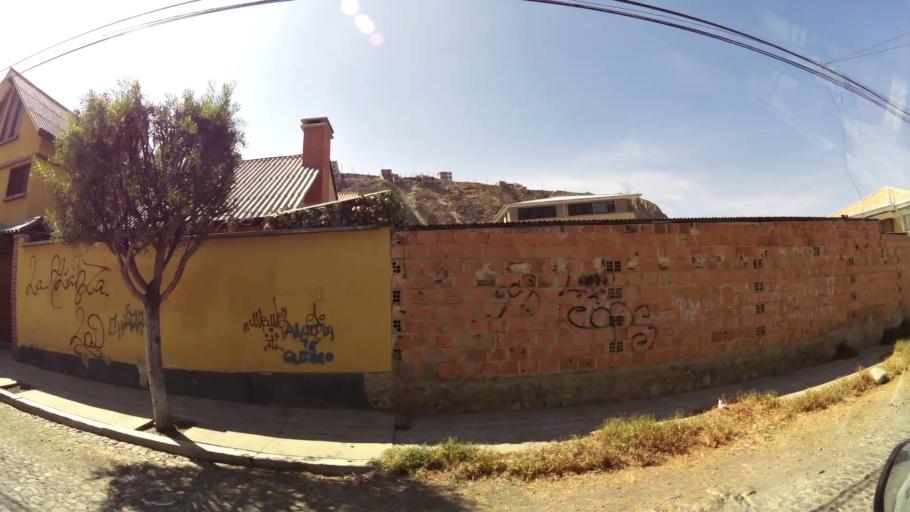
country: BO
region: La Paz
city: La Paz
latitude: -16.5188
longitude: -68.0870
